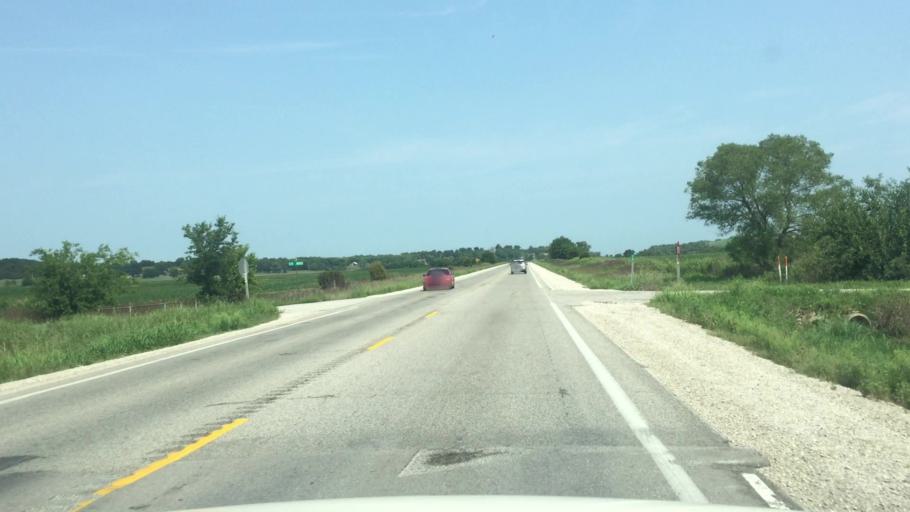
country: US
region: Kansas
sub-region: Montgomery County
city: Cherryvale
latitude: 37.1942
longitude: -95.5814
